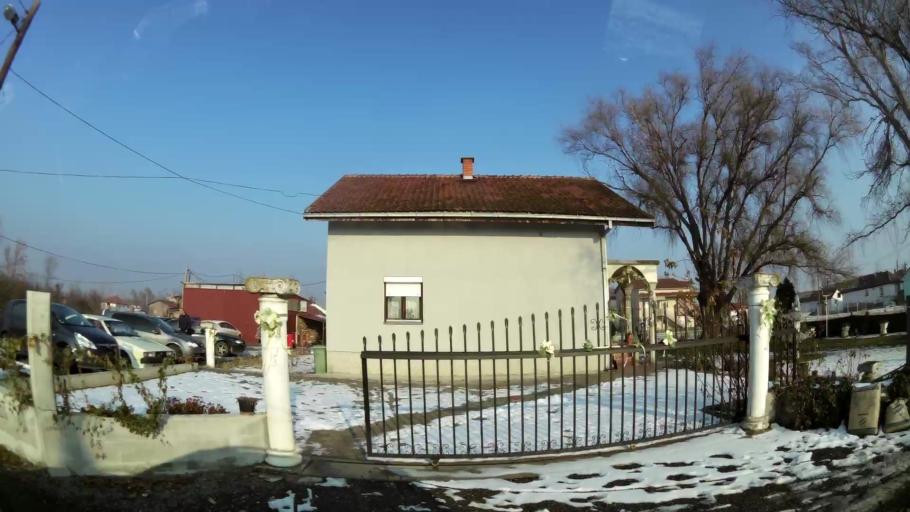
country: MK
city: Kadino
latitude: 41.9642
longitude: 21.5945
